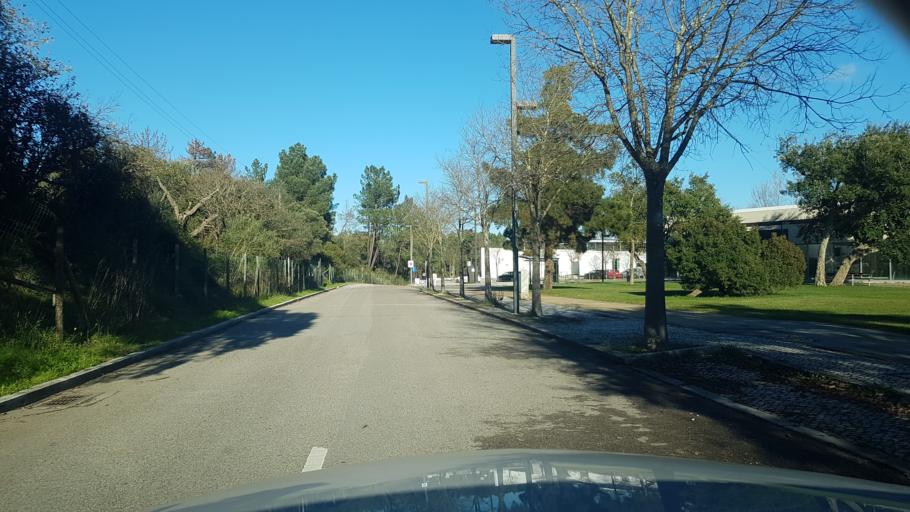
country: PT
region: Santarem
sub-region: Entroncamento
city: Entroncamento
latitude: 39.4771
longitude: -8.4667
